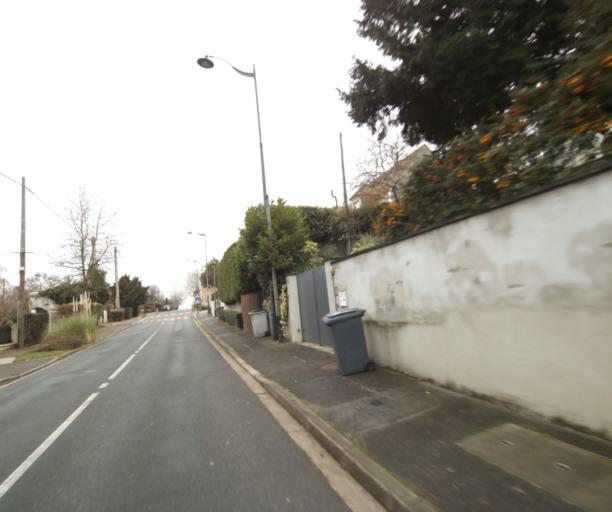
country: FR
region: Ile-de-France
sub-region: Departement des Yvelines
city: Bougival
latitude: 48.8635
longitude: 2.1656
